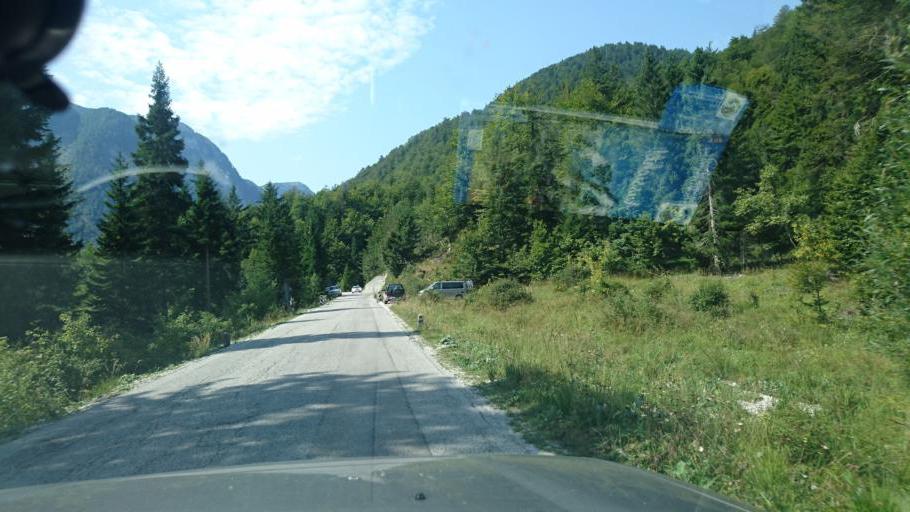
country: SI
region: Bovec
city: Bovec
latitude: 46.4094
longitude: 13.5352
